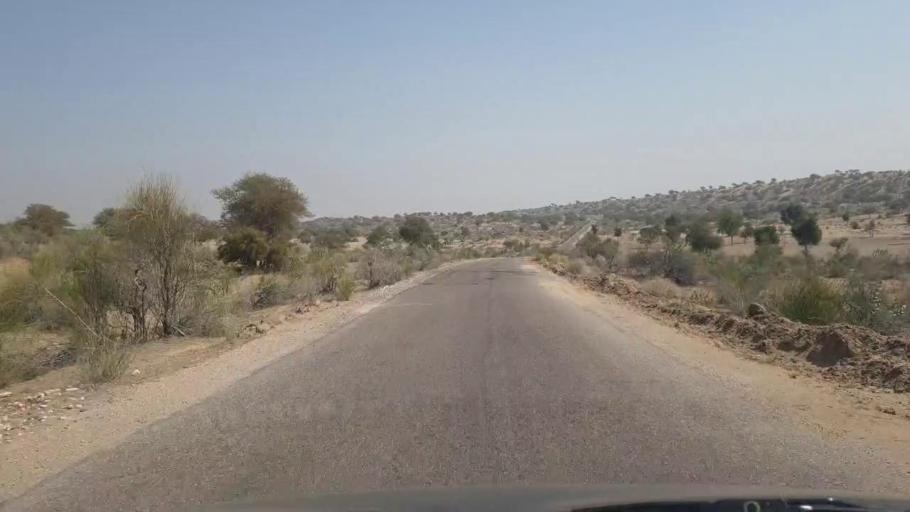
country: PK
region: Sindh
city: Chor
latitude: 25.6569
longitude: 70.1176
